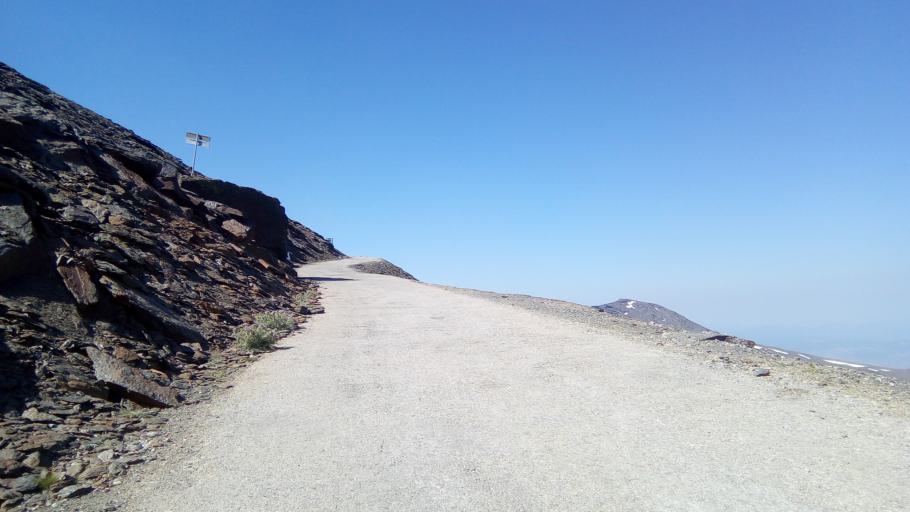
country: ES
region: Andalusia
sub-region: Provincia de Granada
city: Capileira
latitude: 37.0615
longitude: -3.3707
